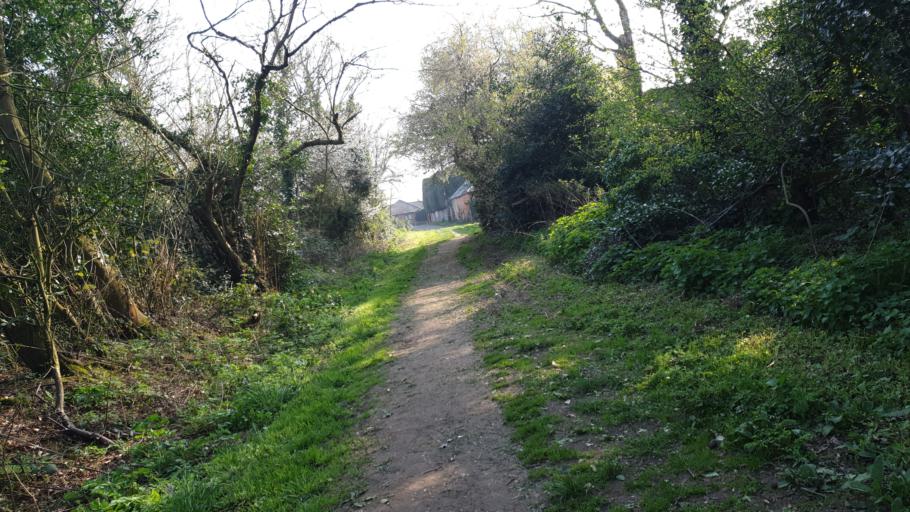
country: GB
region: England
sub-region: Essex
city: Little Clacton
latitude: 51.8759
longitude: 1.1176
